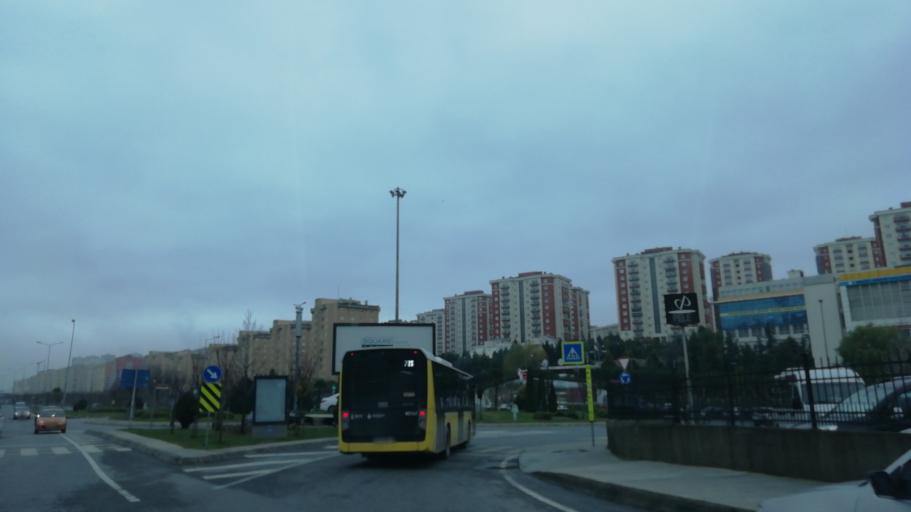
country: TR
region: Istanbul
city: Basaksehir
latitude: 41.0902
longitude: 28.8026
